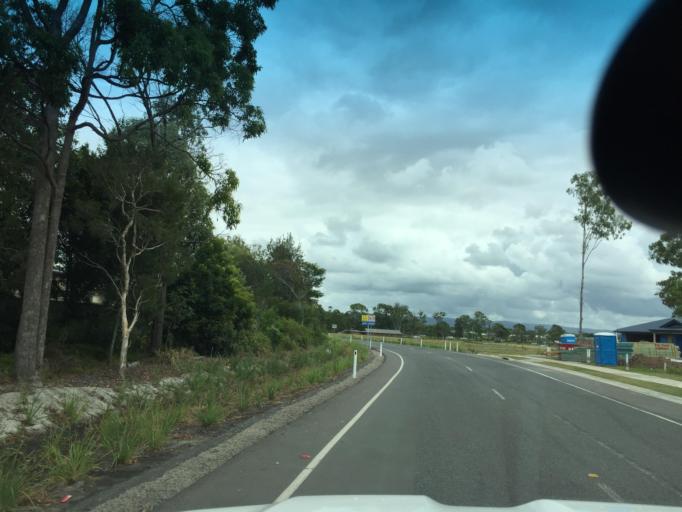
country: AU
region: Queensland
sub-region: Moreton Bay
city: Burpengary
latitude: -27.1649
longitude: 152.9843
